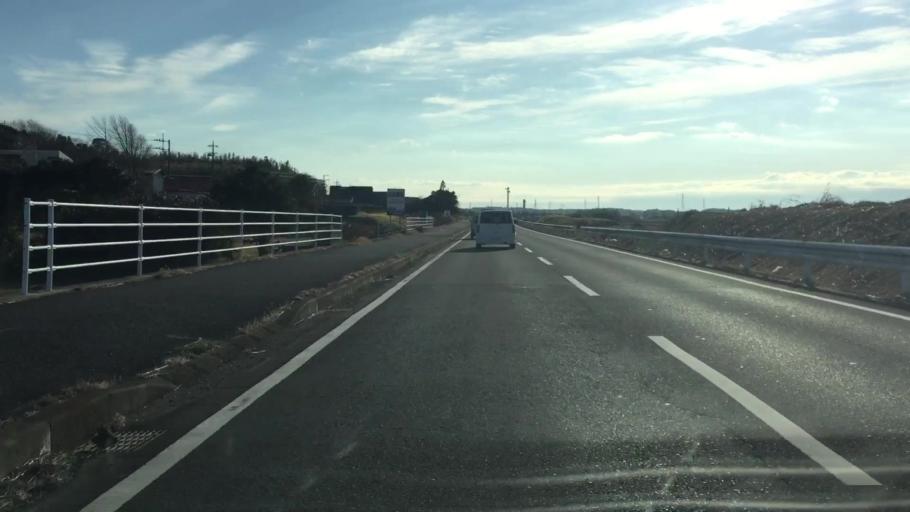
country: JP
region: Ibaraki
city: Toride
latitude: 35.8520
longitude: 140.1244
